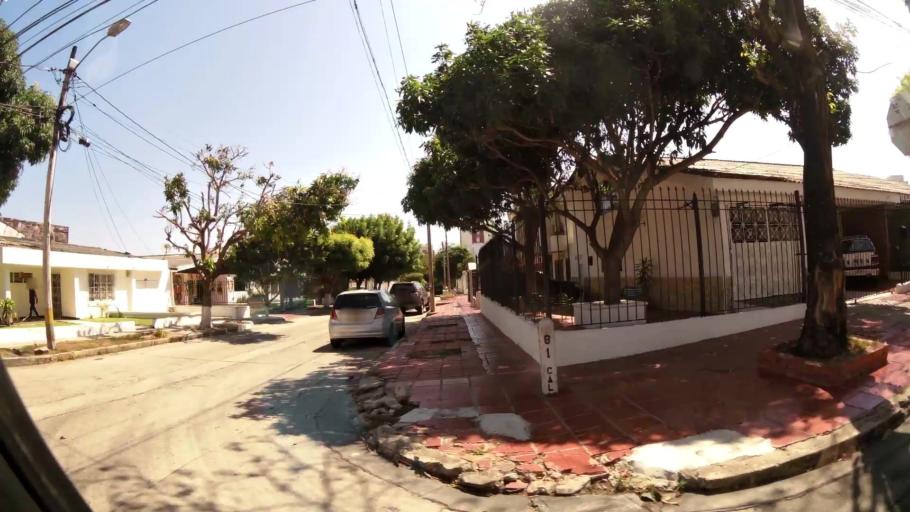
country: CO
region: Atlantico
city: Barranquilla
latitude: 11.0134
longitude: -74.8076
